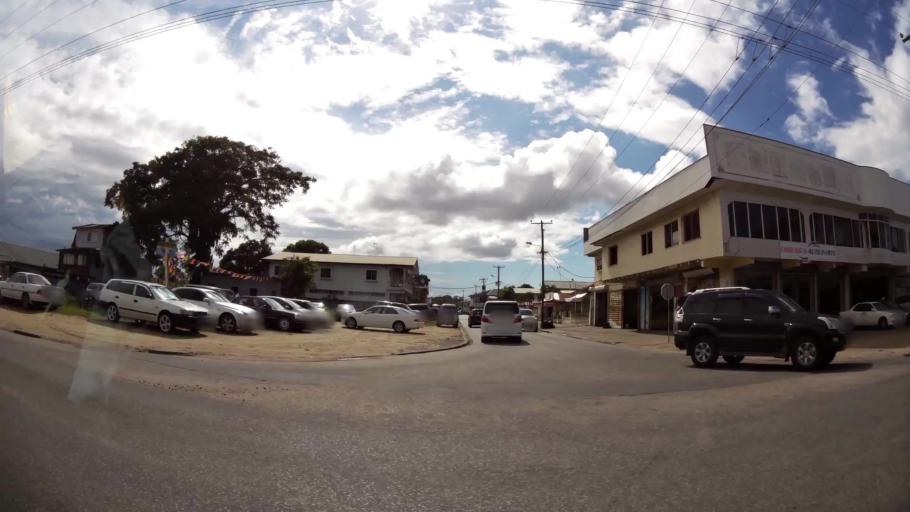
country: SR
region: Paramaribo
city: Paramaribo
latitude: 5.8392
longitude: -55.1514
